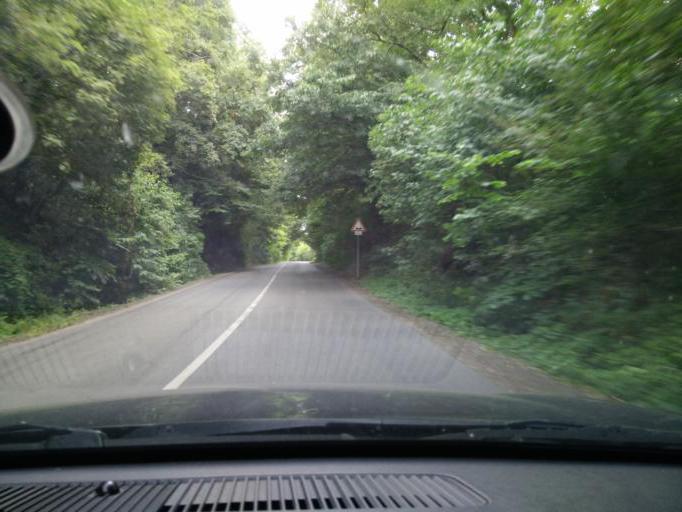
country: HU
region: Komarom-Esztergom
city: Baj
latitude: 47.6637
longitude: 18.3990
